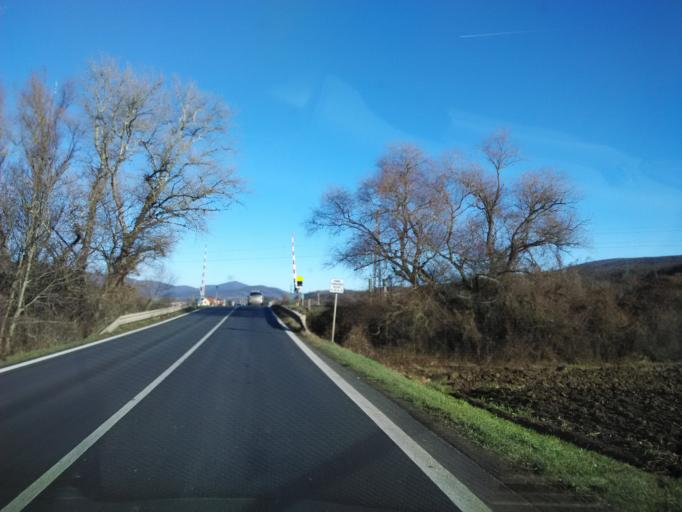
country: SK
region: Nitriansky
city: Tlmace
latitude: 48.2999
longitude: 18.5314
